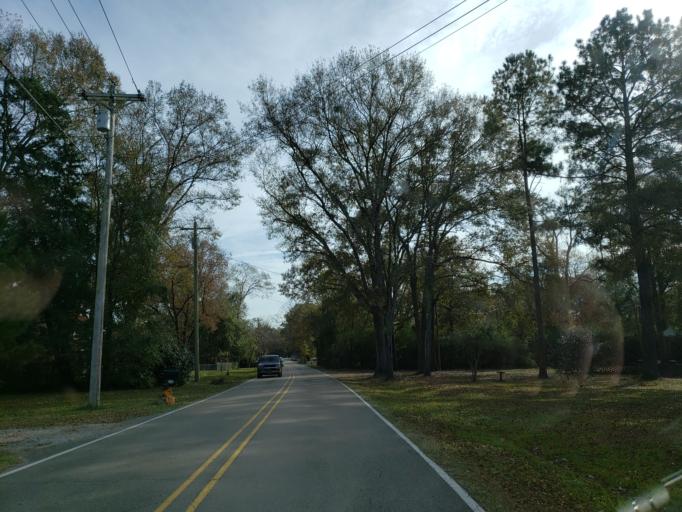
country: US
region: Mississippi
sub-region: Forrest County
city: Rawls Springs
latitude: 31.3829
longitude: -89.3722
